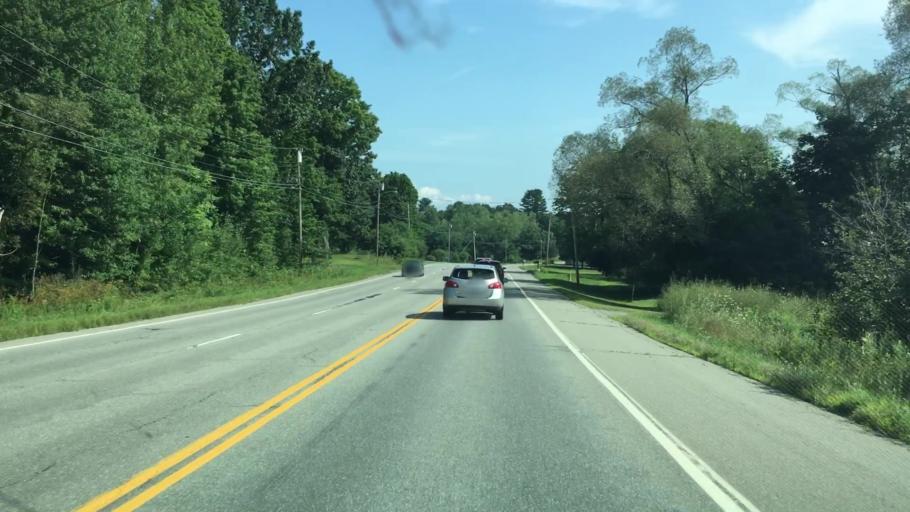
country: US
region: Maine
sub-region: Penobscot County
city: Orrington
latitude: 44.7059
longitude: -68.8461
